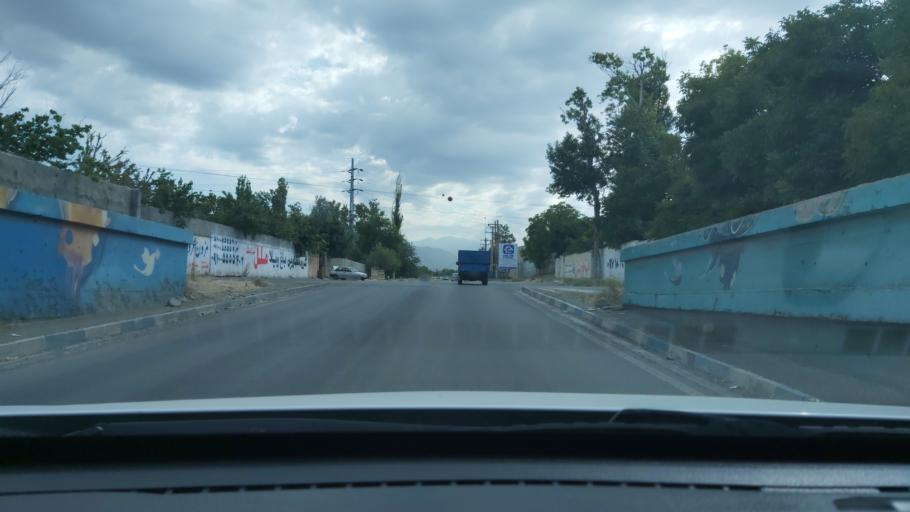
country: IR
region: Alborz
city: Hashtgerd
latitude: 35.9356
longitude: 50.7583
